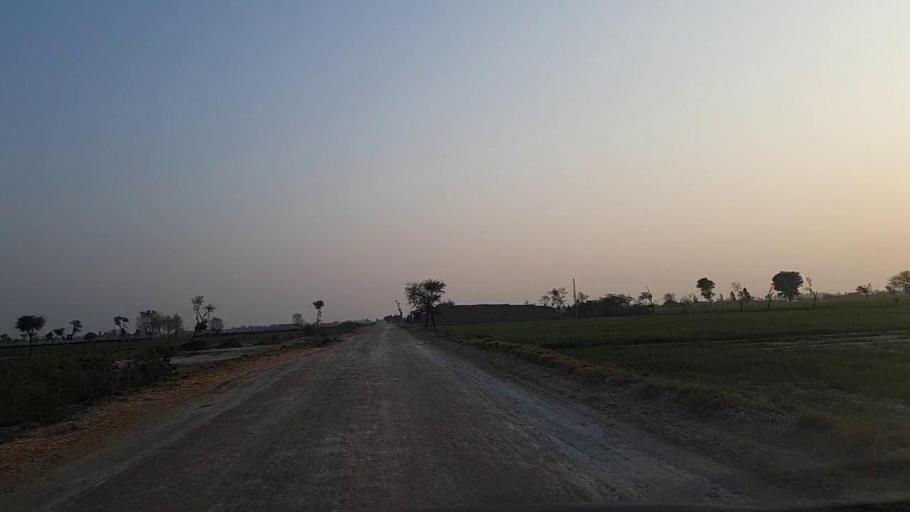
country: PK
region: Sindh
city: Daur
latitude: 26.4303
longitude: 68.3680
